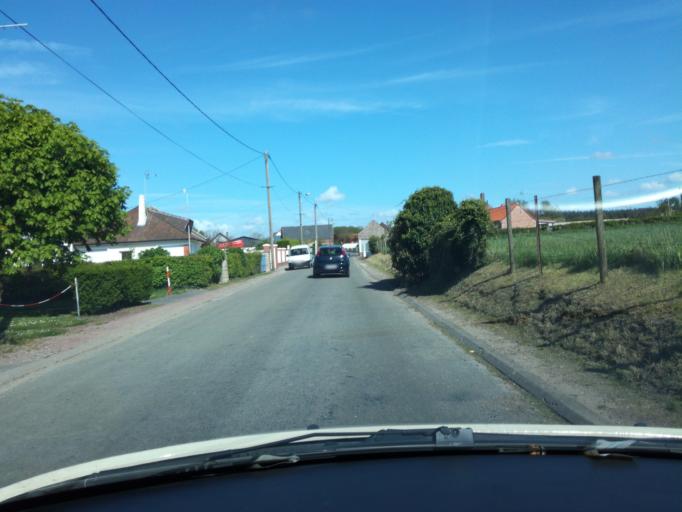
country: FR
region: Picardie
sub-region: Departement de la Somme
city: Pende
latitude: 50.1598
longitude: 1.5922
